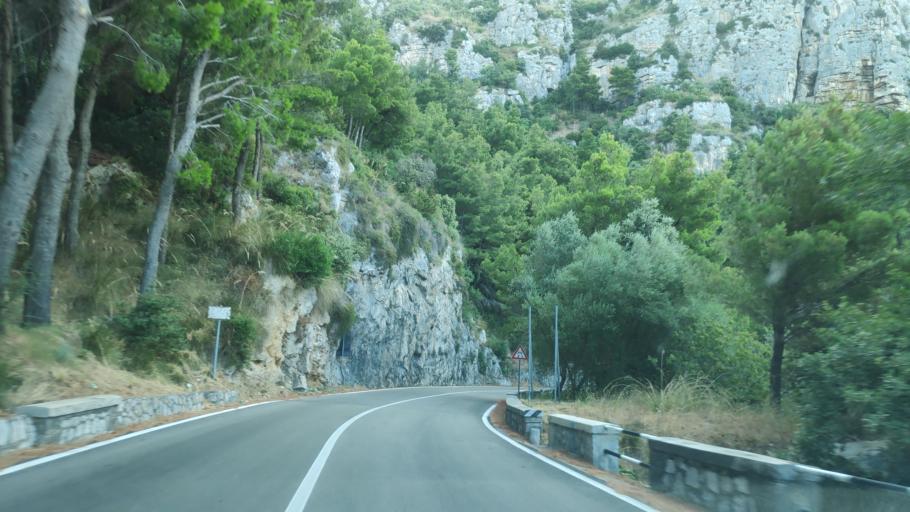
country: IT
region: Campania
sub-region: Provincia di Napoli
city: Arola-Preazzano
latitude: 40.6158
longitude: 14.4364
